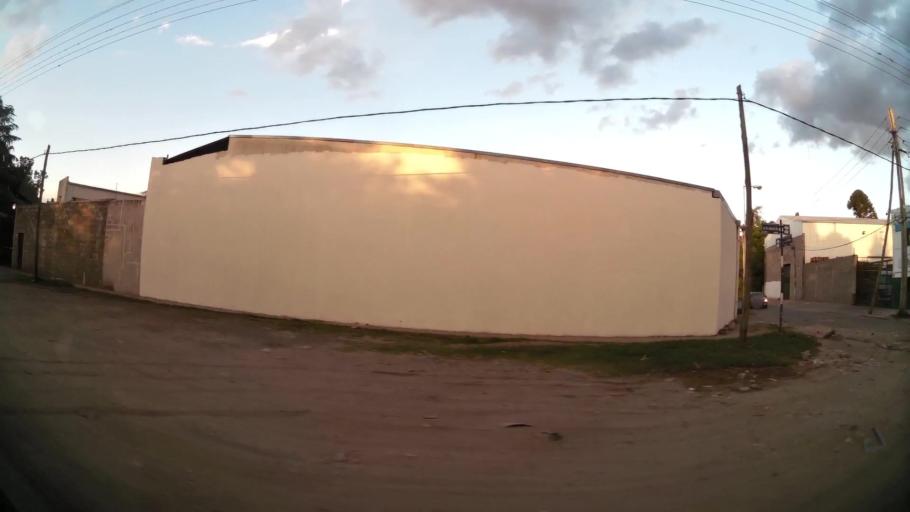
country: AR
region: Buenos Aires
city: Santa Catalina - Dique Lujan
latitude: -34.4939
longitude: -58.7628
